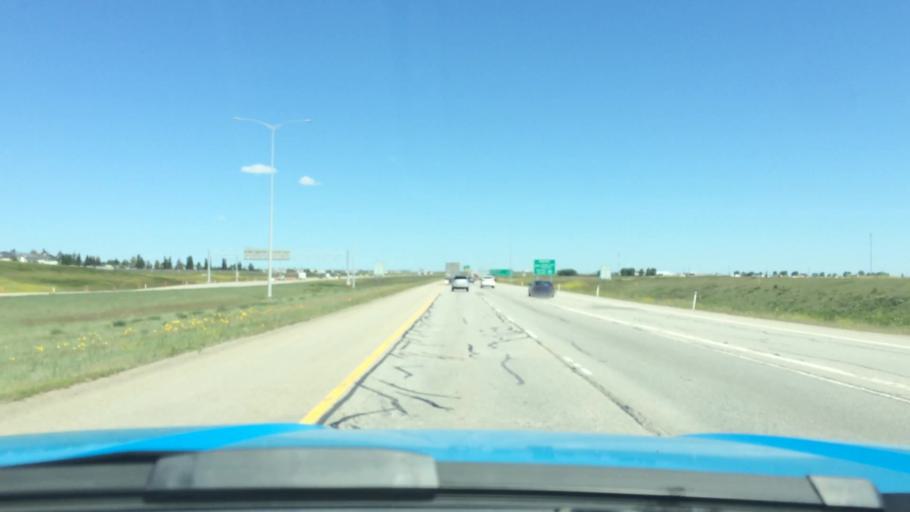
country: CA
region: Alberta
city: Chestermere
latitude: 51.0729
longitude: -113.9202
